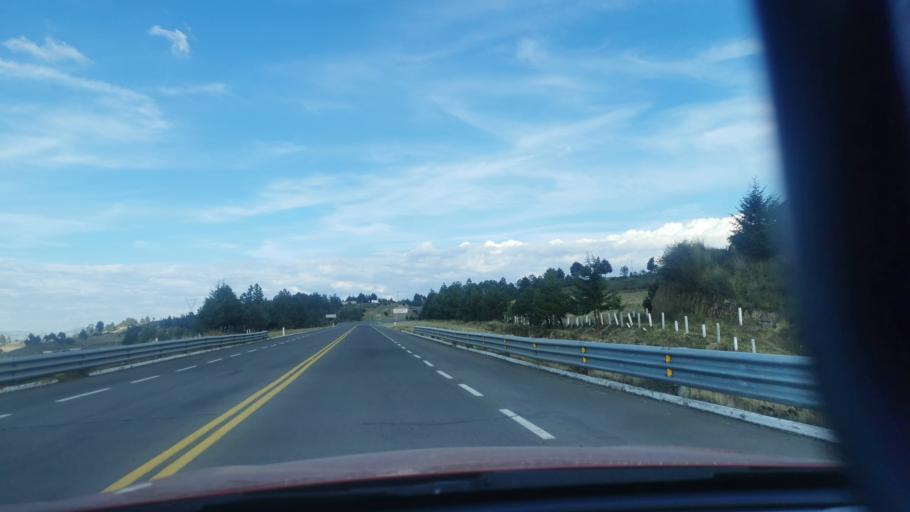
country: MX
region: Mexico
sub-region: Villa Victoria
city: Colonia Doctor Gustavo Baz
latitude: 19.3596
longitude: -99.9556
